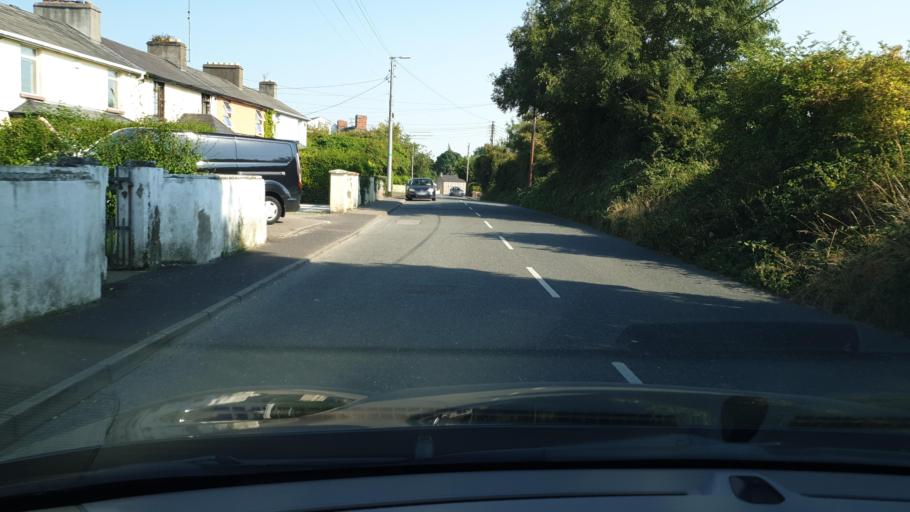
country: IE
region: Leinster
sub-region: An Mhi
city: Navan
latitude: 53.6575
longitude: -6.6838
